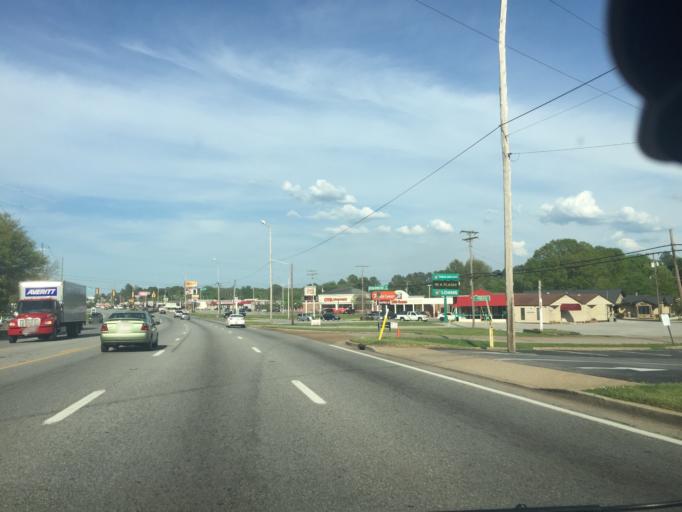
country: US
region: Tennessee
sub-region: Hamilton County
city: East Chattanooga
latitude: 35.0856
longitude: -85.1932
